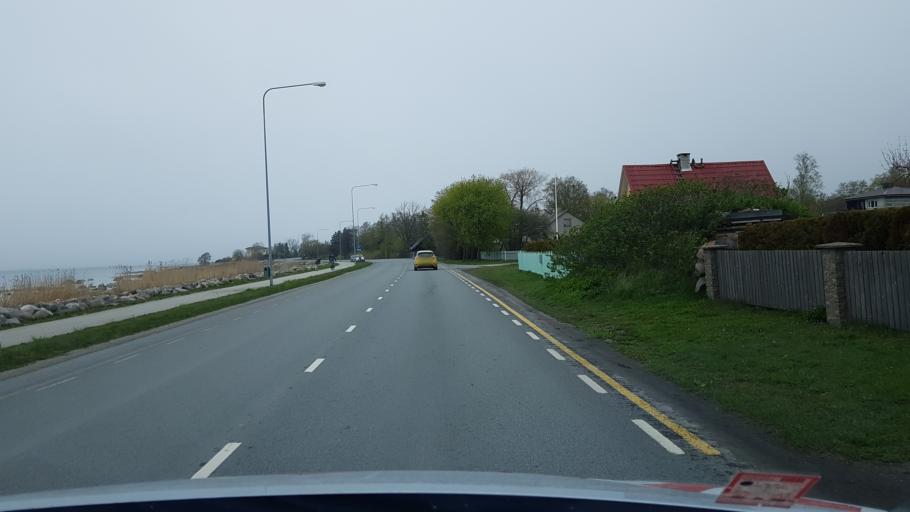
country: EE
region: Harju
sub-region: Viimsi vald
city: Rummu
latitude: 59.5511
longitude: 24.7952
